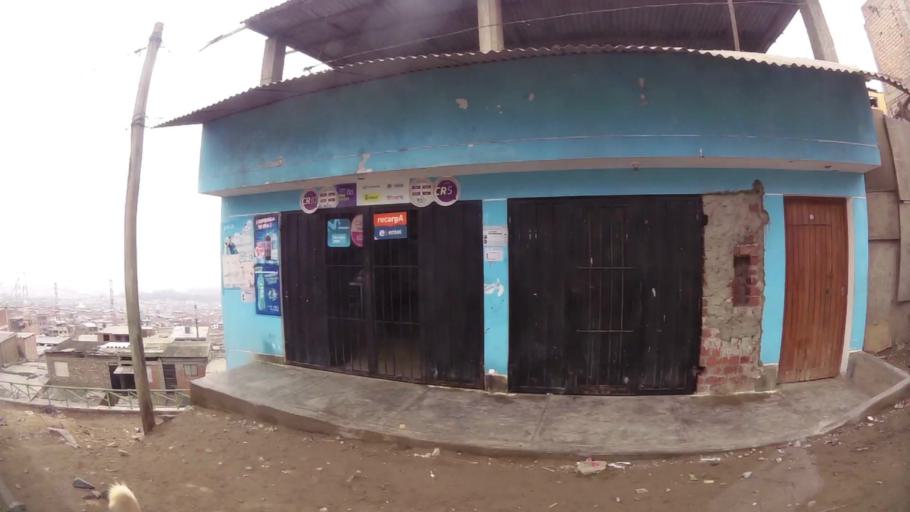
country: PE
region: Lima
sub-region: Lima
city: Surco
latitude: -12.1792
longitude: -76.9556
